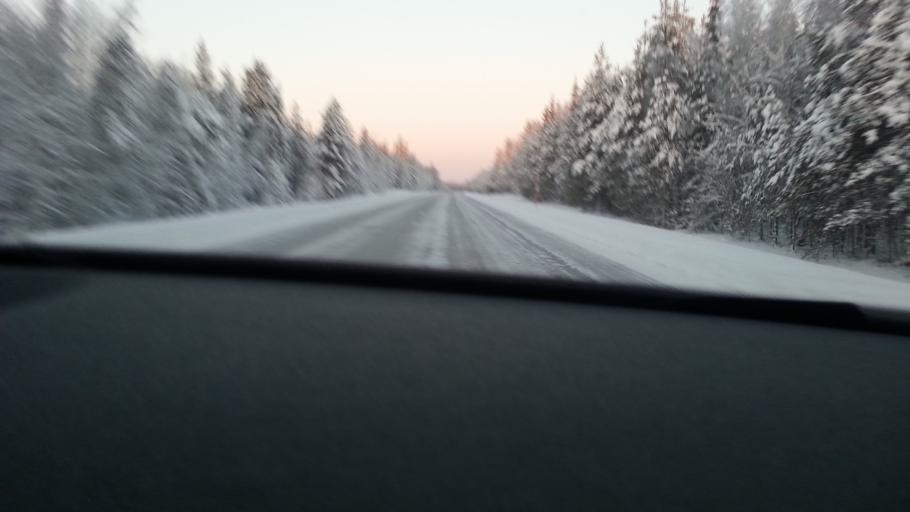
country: FI
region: Lapland
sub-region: Tunturi-Lappi
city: Kittilae
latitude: 67.2196
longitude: 24.9238
